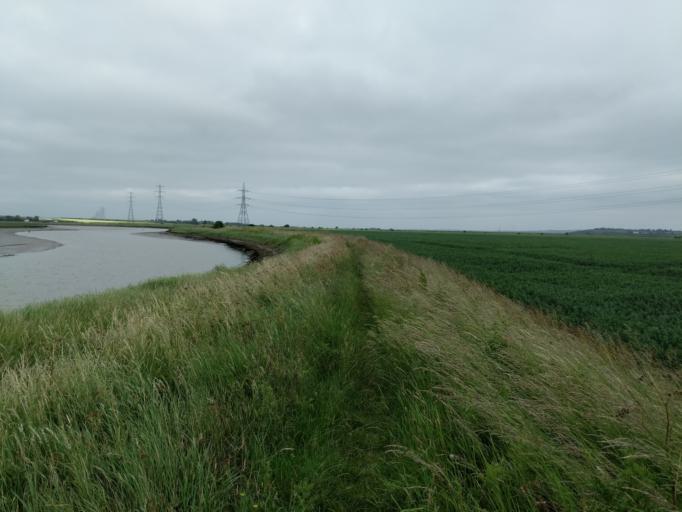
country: GB
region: England
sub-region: Kent
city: Faversham
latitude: 51.3351
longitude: 0.9111
